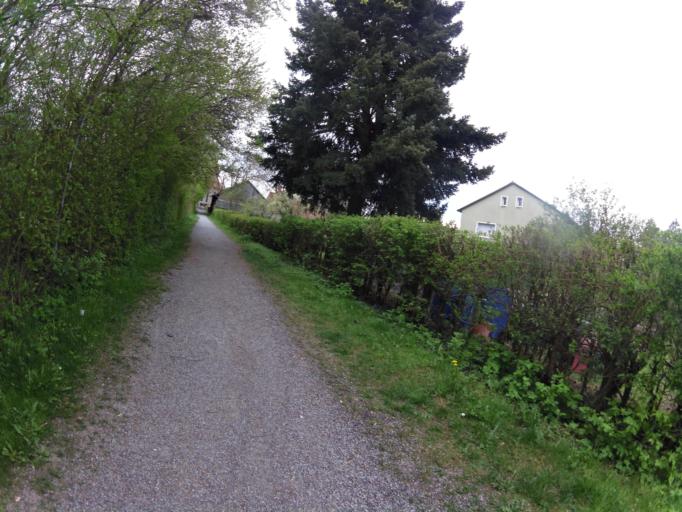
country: DE
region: Bavaria
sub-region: Regierungsbezirk Unterfranken
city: Giebelstadt
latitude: 49.6554
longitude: 9.9451
